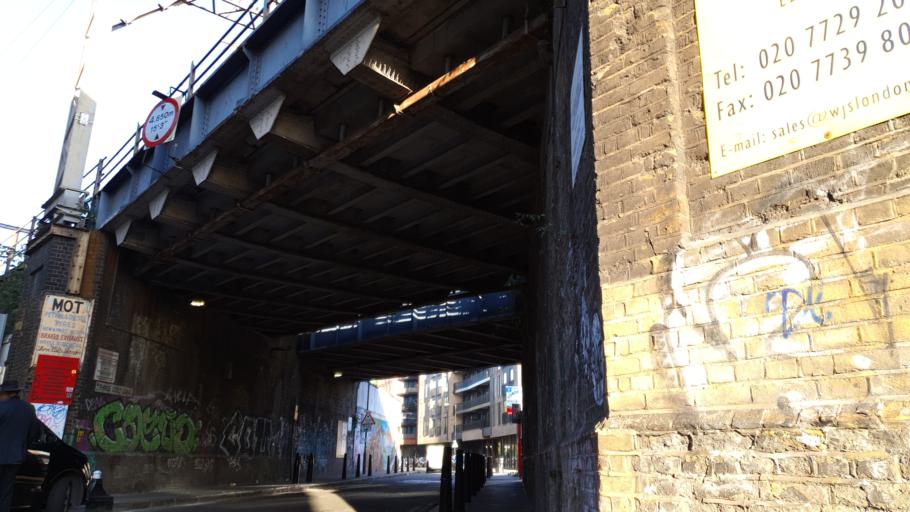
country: GB
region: England
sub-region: Greater London
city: Bethnal Green
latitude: 51.5245
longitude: -0.0574
